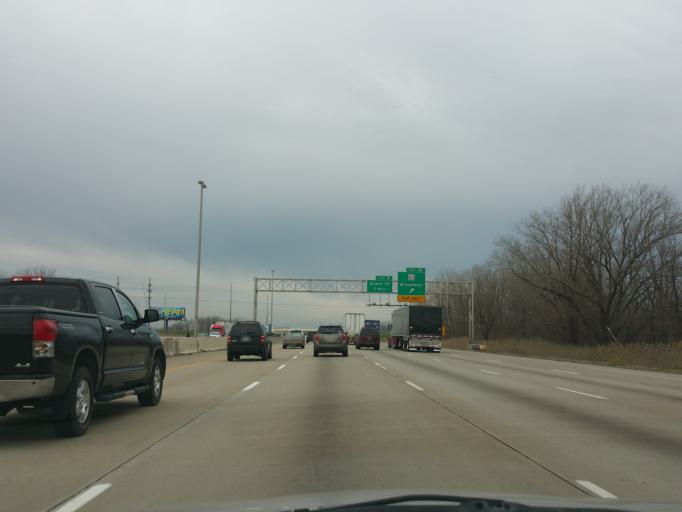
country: US
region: Indiana
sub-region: Lake County
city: Gary
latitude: 41.5675
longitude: -87.3294
